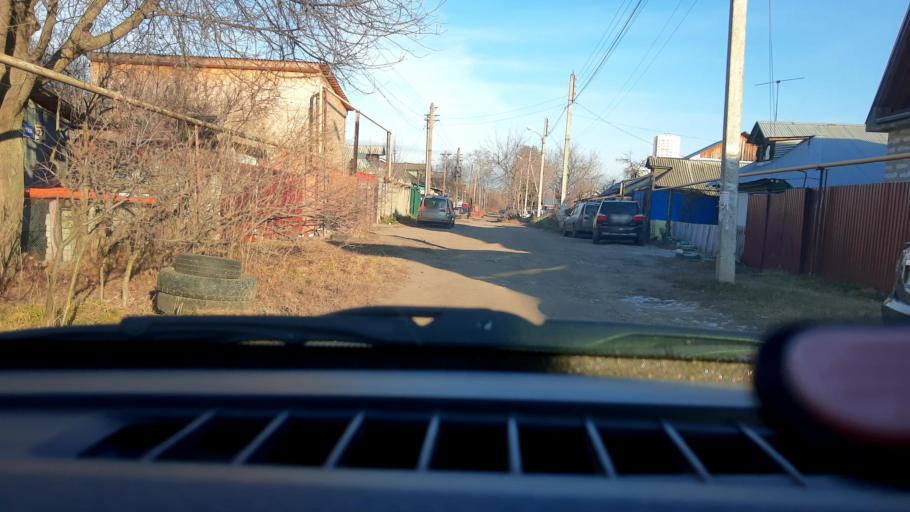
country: RU
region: Nizjnij Novgorod
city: Nizhniy Novgorod
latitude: 56.2967
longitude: 43.9167
